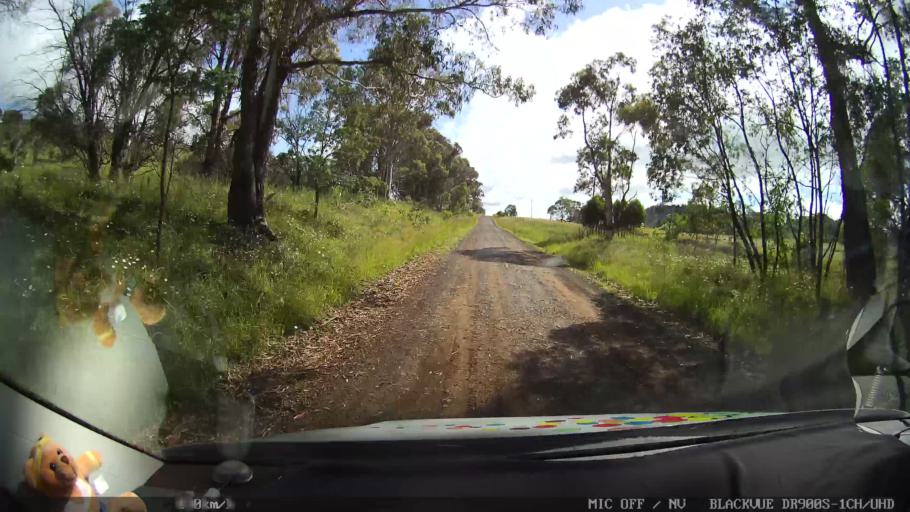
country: AU
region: New South Wales
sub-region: Guyra
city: Guyra
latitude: -30.0089
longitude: 151.6628
